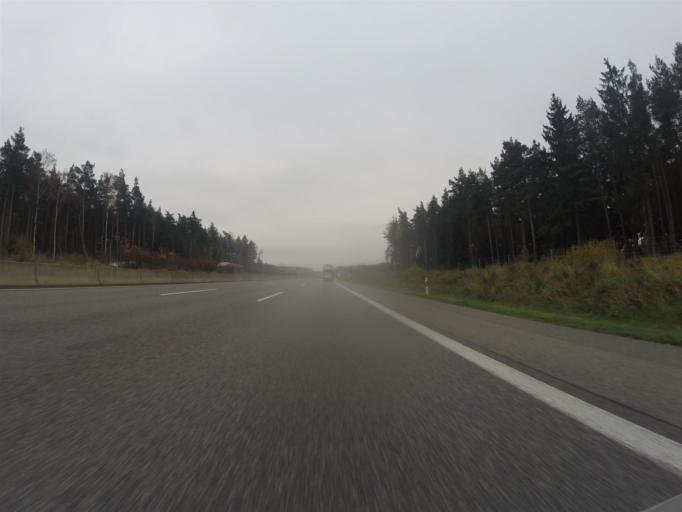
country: DE
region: Thuringia
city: Hermsdorf
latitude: 50.9150
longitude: 11.8410
